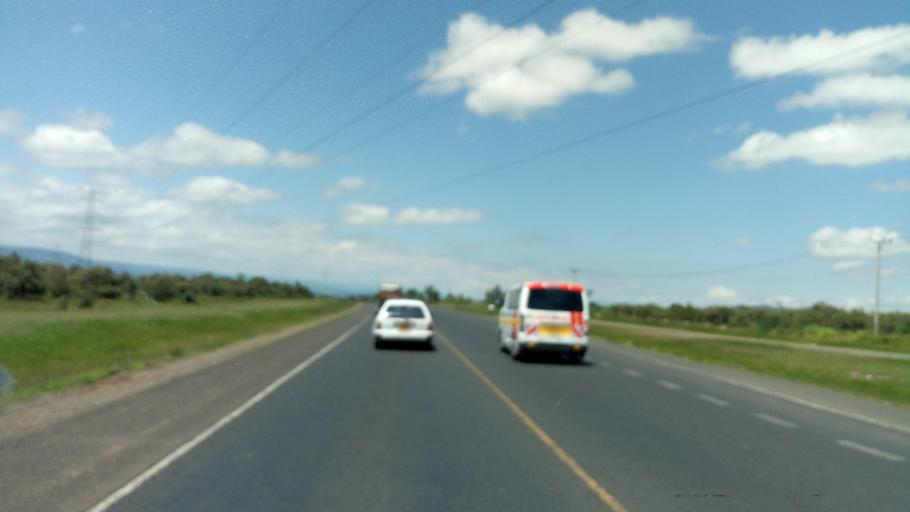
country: KE
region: Nakuru
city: Naivasha
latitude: -0.5378
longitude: 36.3355
